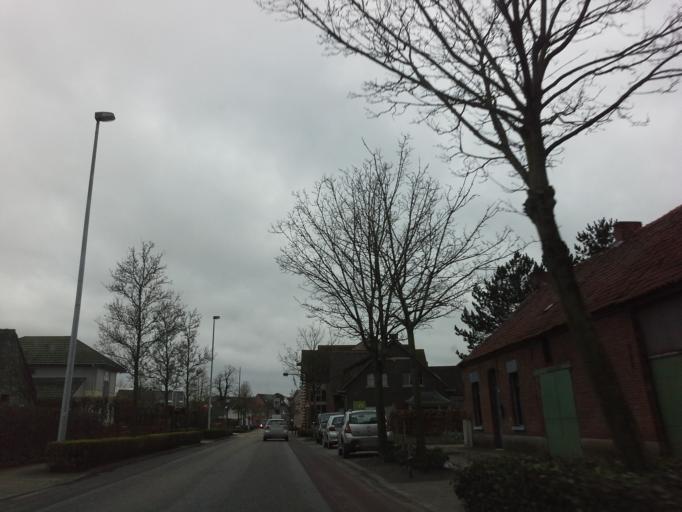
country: BE
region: Flanders
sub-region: Provincie Antwerpen
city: Olen
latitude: 51.1213
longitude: 4.8218
